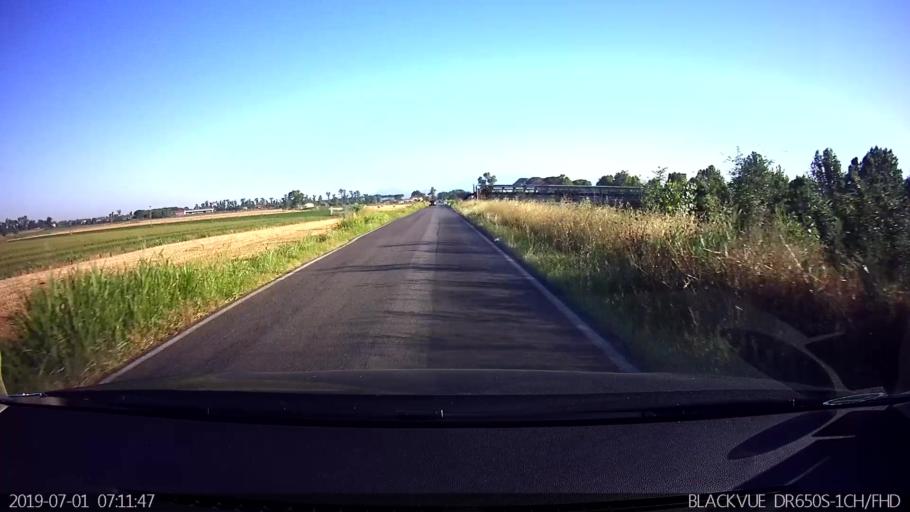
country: IT
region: Latium
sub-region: Provincia di Latina
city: Borgo Hermada
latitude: 41.3238
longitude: 13.1764
